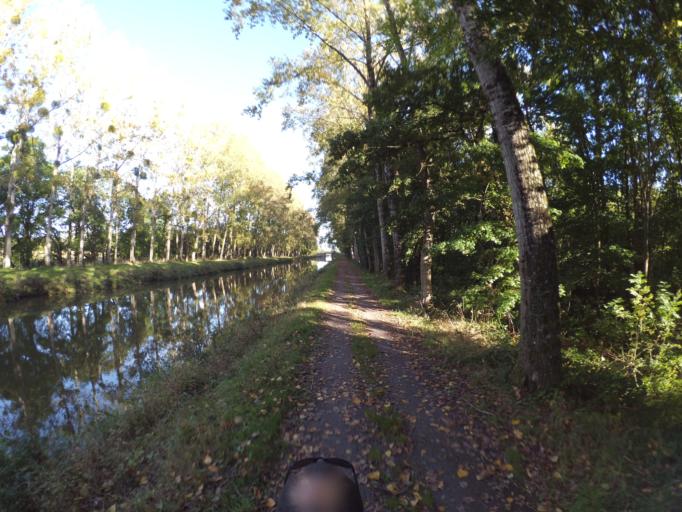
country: FR
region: Brittany
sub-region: Departement du Morbihan
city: Saint-Vincent-sur-Oust
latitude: 47.7211
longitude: -2.1736
